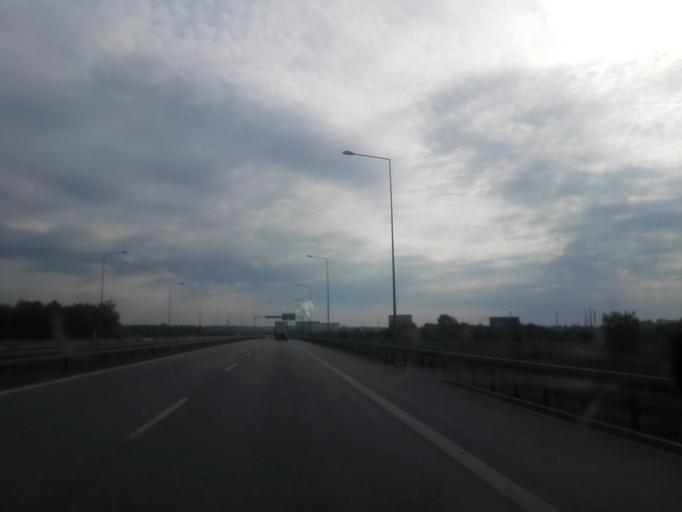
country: PL
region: Lodz Voivodeship
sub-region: Powiat tomaszowski
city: Tomaszow Mazowiecki
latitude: 51.5476
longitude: 19.9825
